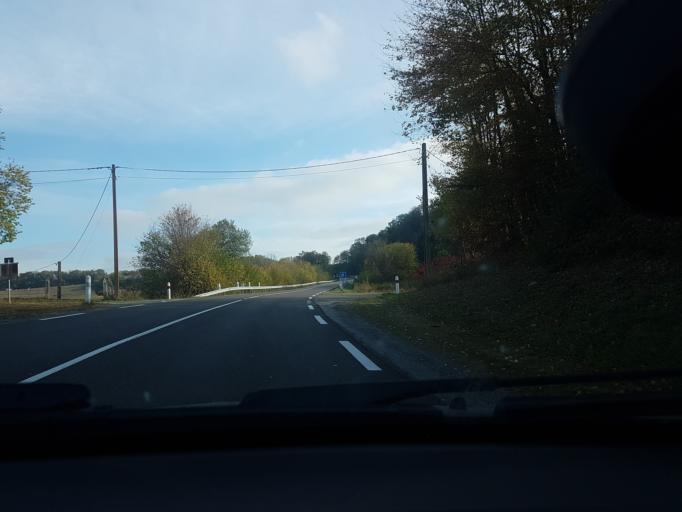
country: FR
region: Franche-Comte
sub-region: Departement de la Haute-Saone
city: Frahier-et-Chatebier
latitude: 47.6539
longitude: 6.7579
